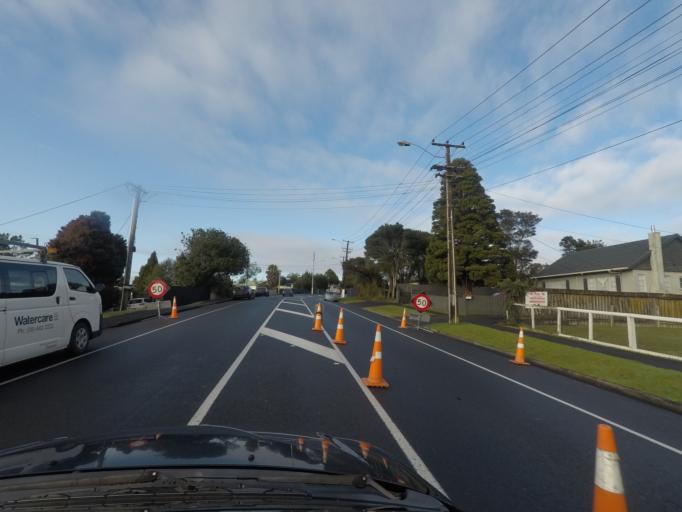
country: NZ
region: Auckland
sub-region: Auckland
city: Waitakere
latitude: -36.8959
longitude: 174.6194
